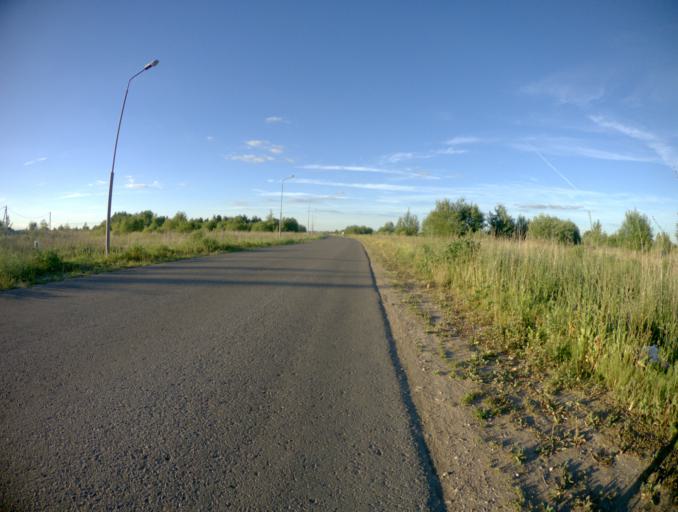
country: RU
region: Vladimir
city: Bogolyubovo
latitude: 56.1913
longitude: 40.5087
